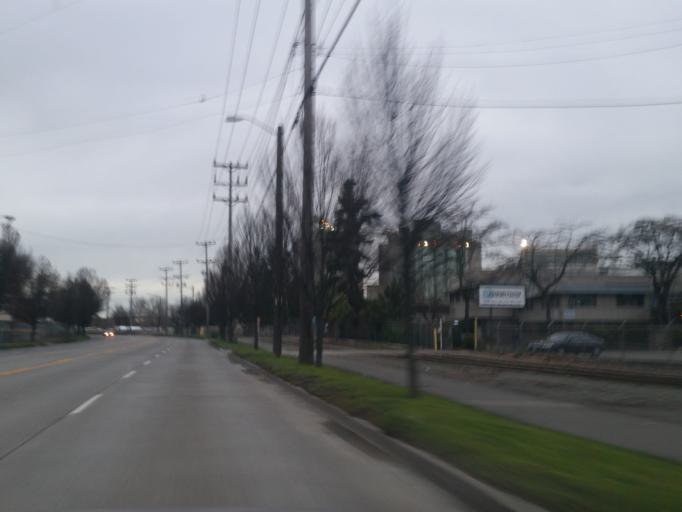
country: US
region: Washington
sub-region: King County
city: White Center
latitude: 47.5521
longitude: -122.3463
